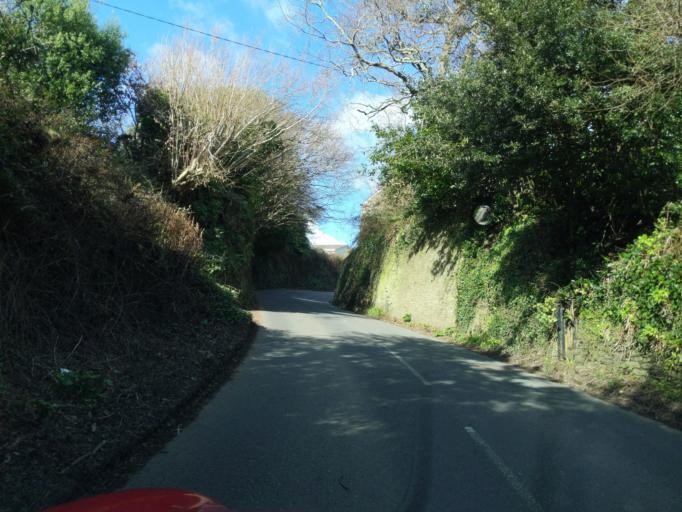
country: GB
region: England
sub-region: Devon
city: Kingsbridge
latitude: 50.2893
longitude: -3.7707
